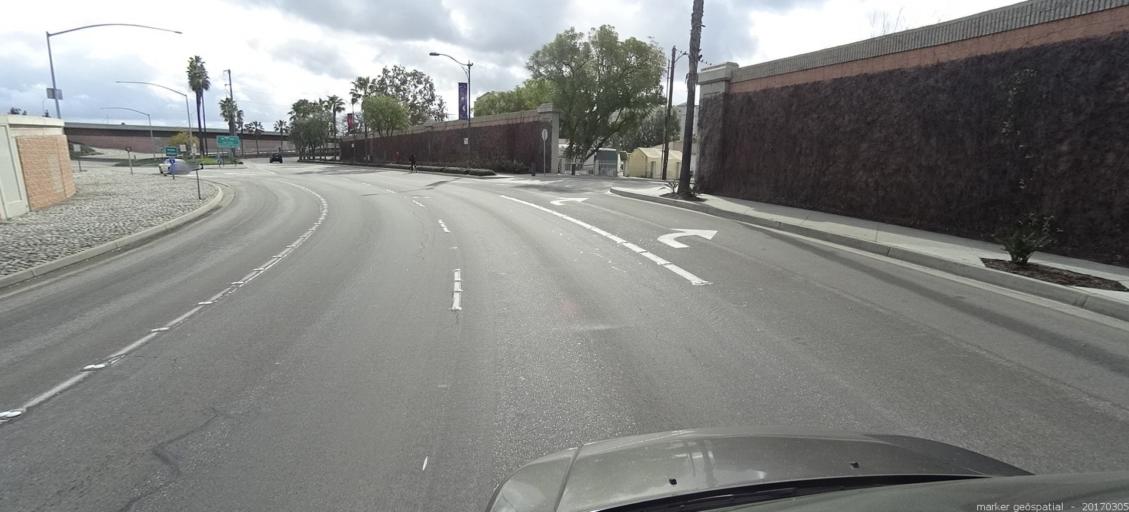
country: US
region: California
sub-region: Orange County
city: Anaheim
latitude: 33.8021
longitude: -117.9039
